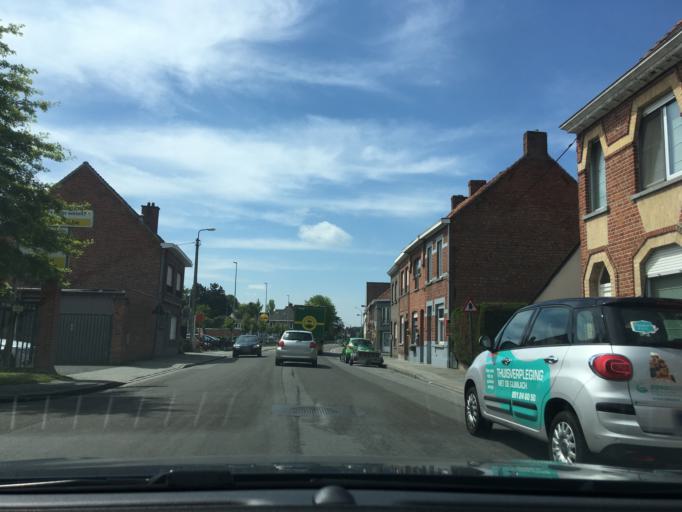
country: BE
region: Flanders
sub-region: Provincie West-Vlaanderen
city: Izegem
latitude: 50.9203
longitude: 3.2002
